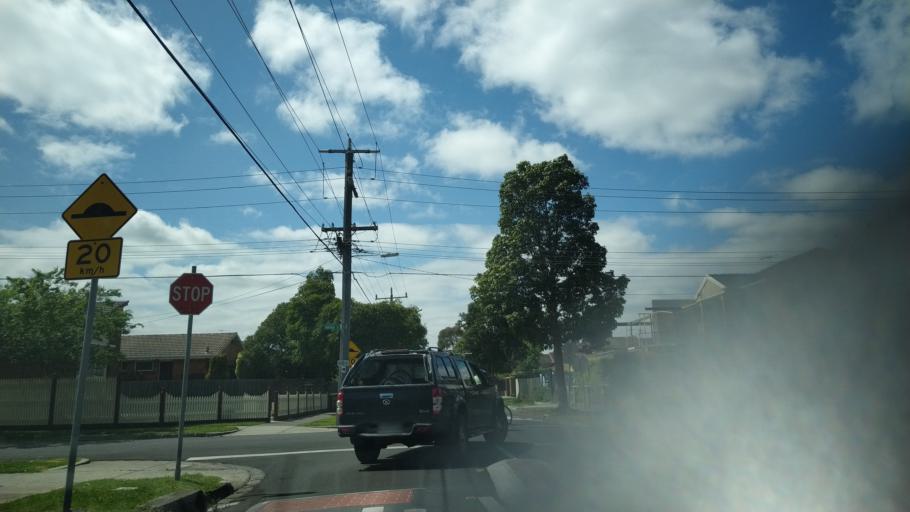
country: AU
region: Victoria
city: Murrumbeena
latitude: -37.8970
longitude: 145.0611
